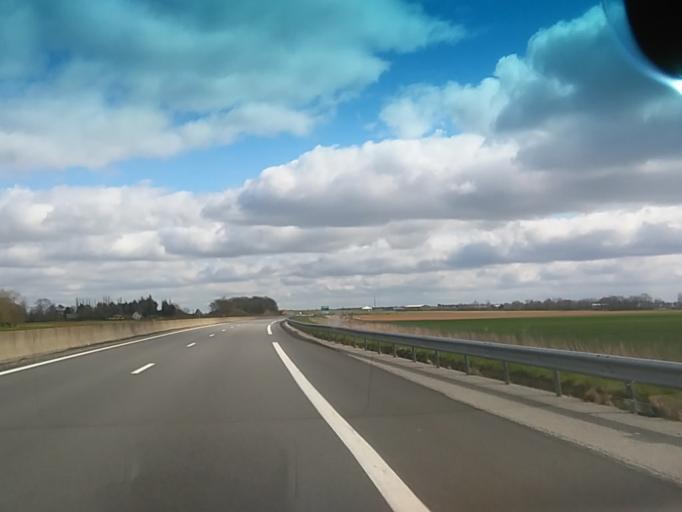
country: FR
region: Haute-Normandie
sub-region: Departement de l'Eure
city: Bernay
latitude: 49.1403
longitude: 0.5561
